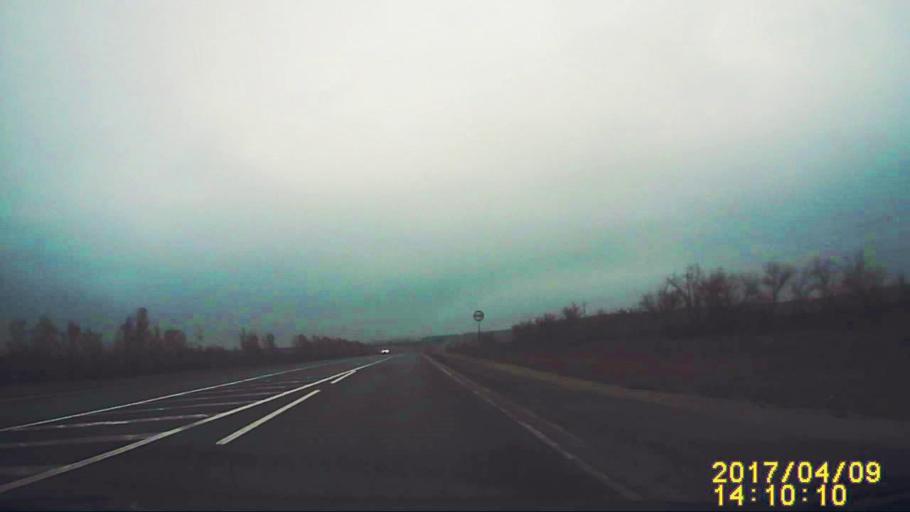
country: RU
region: Ulyanovsk
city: Krasnyy Gulyay
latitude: 54.0356
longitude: 48.2127
